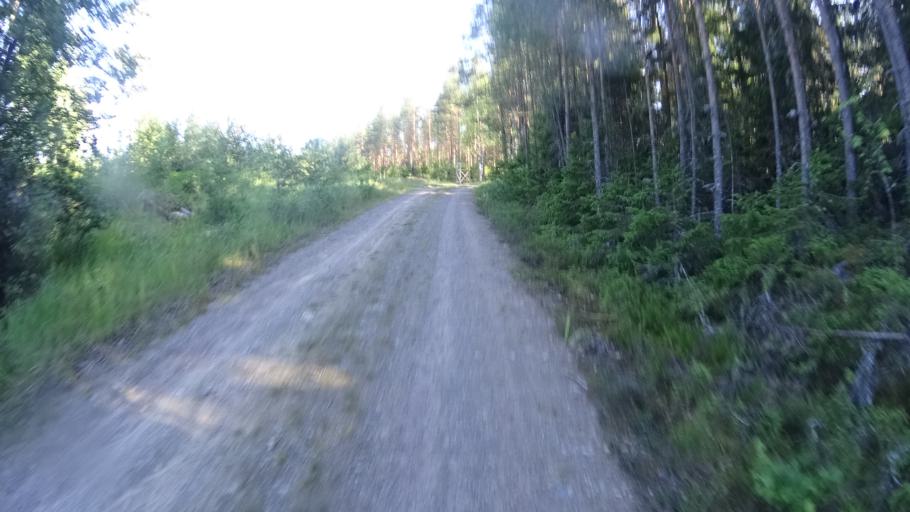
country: FI
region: Uusimaa
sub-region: Helsinki
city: Karkkila
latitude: 60.6582
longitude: 24.1313
